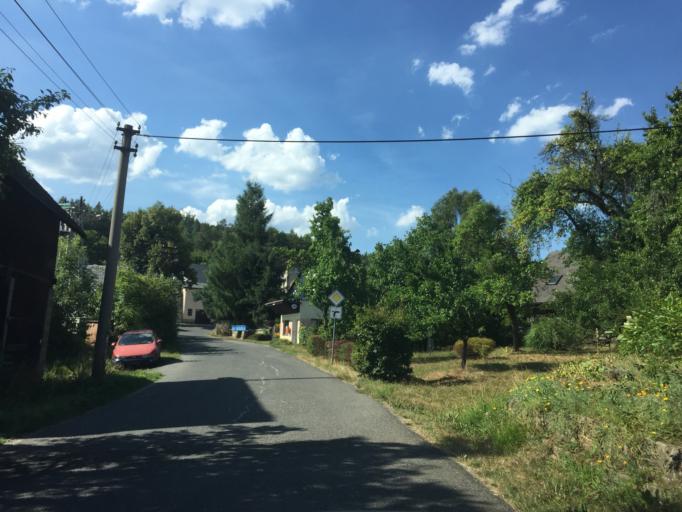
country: CZ
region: Liberecky
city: Mala Skala
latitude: 50.6266
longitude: 15.2109
